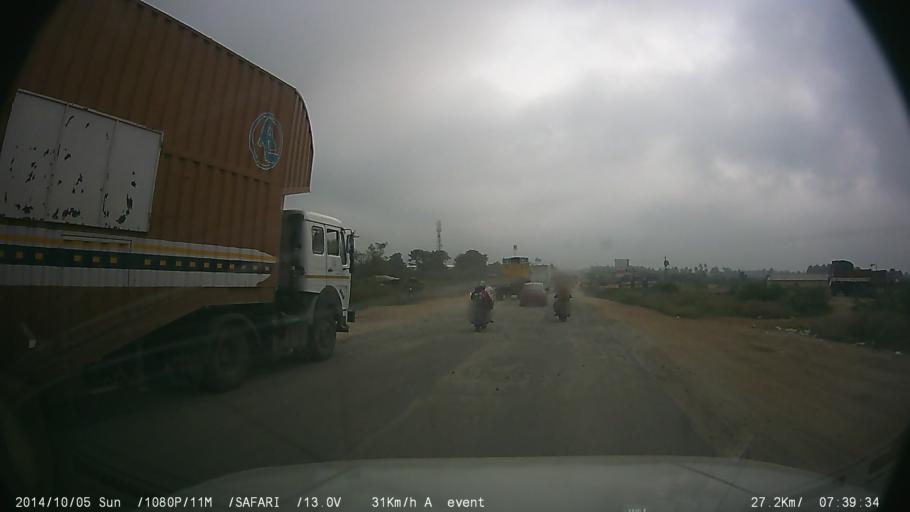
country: IN
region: Tamil Nadu
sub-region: Coimbatore
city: Madukkarai
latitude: 10.8847
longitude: 76.9114
